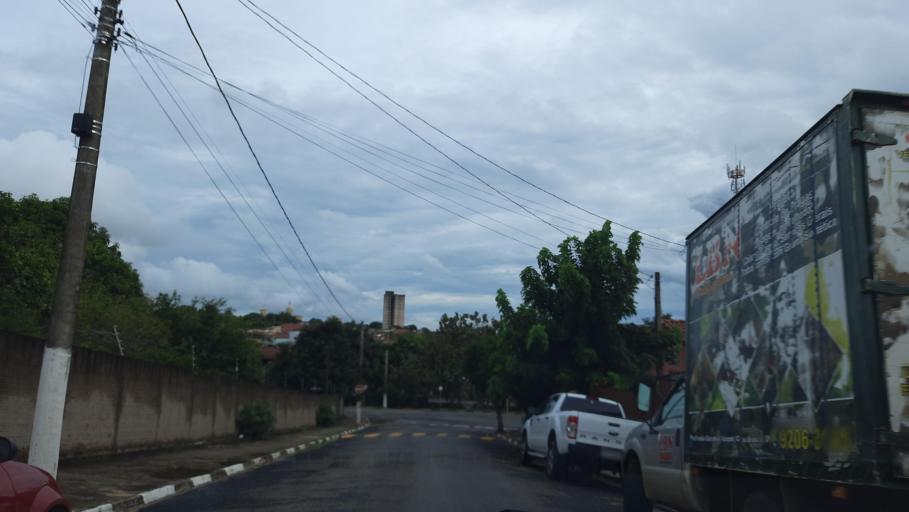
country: BR
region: Sao Paulo
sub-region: Casa Branca
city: Casa Branca
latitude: -21.7668
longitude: -47.0912
